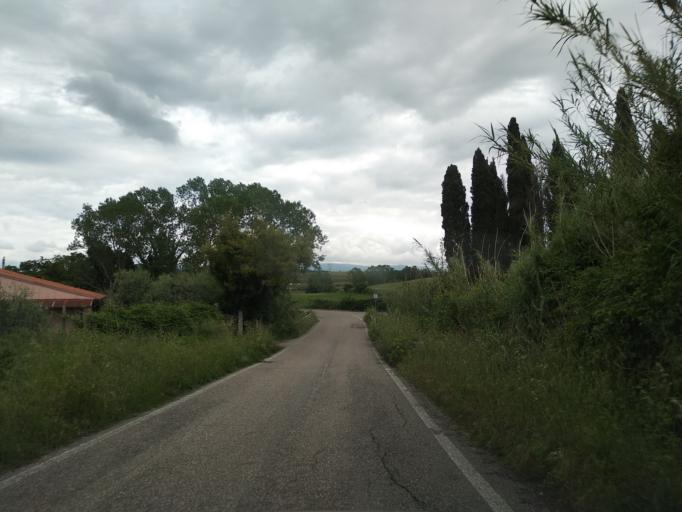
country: IT
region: Tuscany
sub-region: Provincia di Livorno
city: Collesalvetti
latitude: 43.5392
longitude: 10.4578
